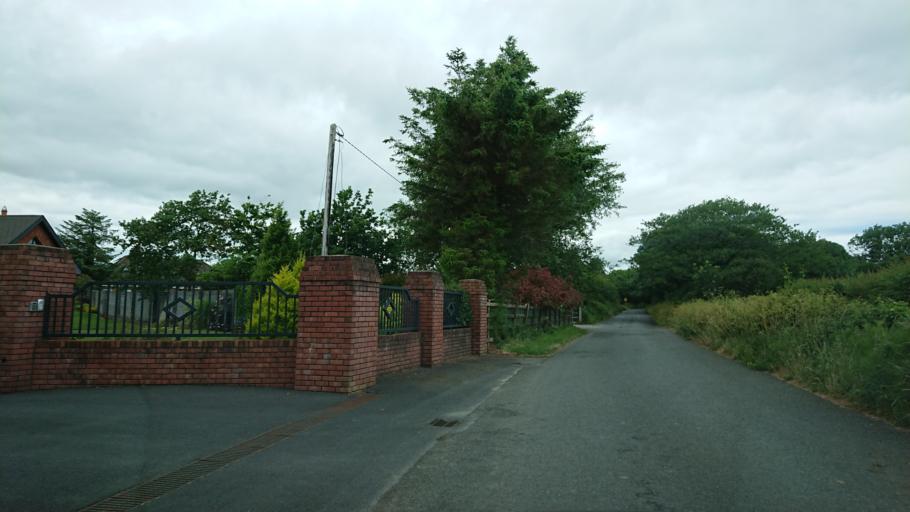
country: IE
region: Munster
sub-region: Waterford
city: Waterford
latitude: 52.2253
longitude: -7.1468
